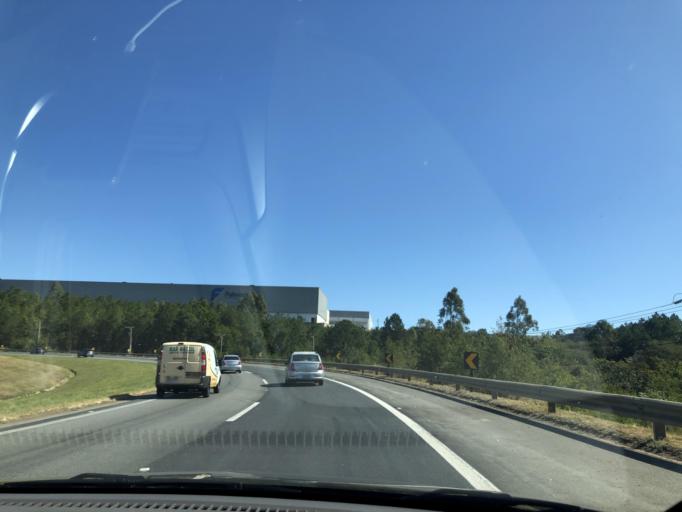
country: BR
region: Sao Paulo
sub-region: Sorocaba
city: Sorocaba
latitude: -23.4425
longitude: -47.3857
